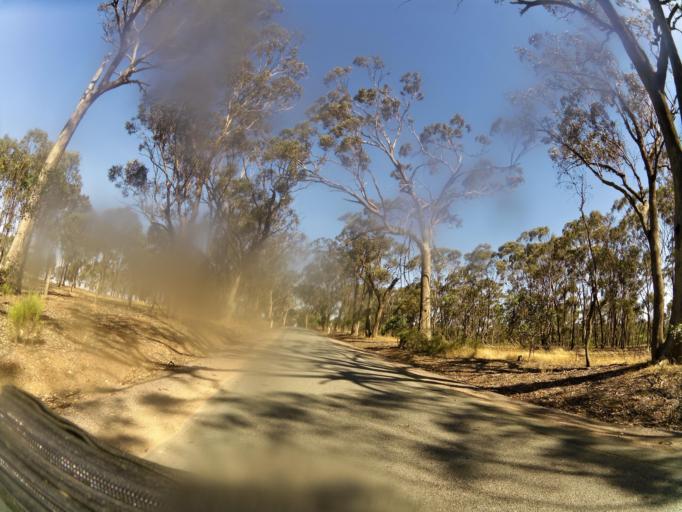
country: AU
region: Victoria
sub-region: Campaspe
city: Kyabram
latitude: -36.8811
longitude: 145.0924
